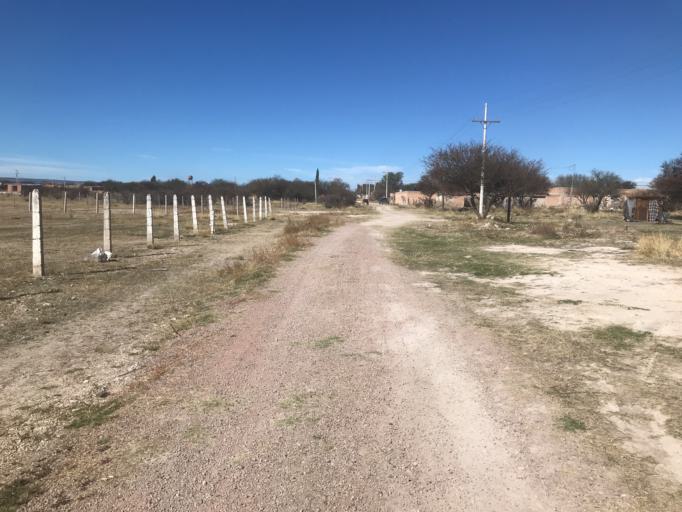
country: MX
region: Durango
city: Victoria de Durango
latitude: 24.0186
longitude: -104.5847
